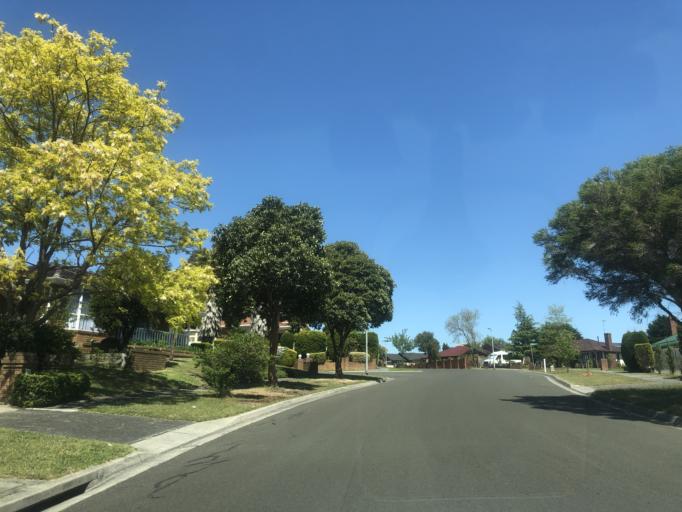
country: AU
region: Victoria
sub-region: Casey
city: Endeavour Hills
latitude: -37.9734
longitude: 145.2709
